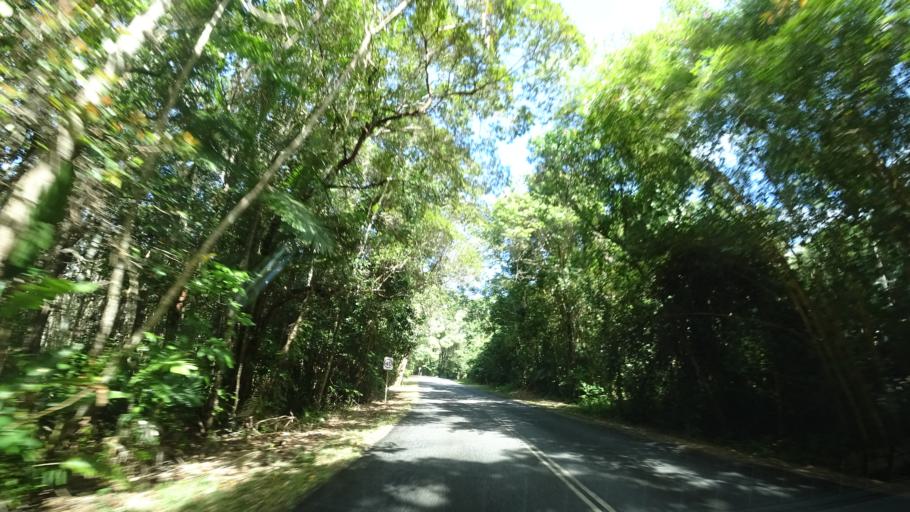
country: AU
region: Queensland
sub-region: Cairns
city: Port Douglas
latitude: -16.2559
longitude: 145.4026
